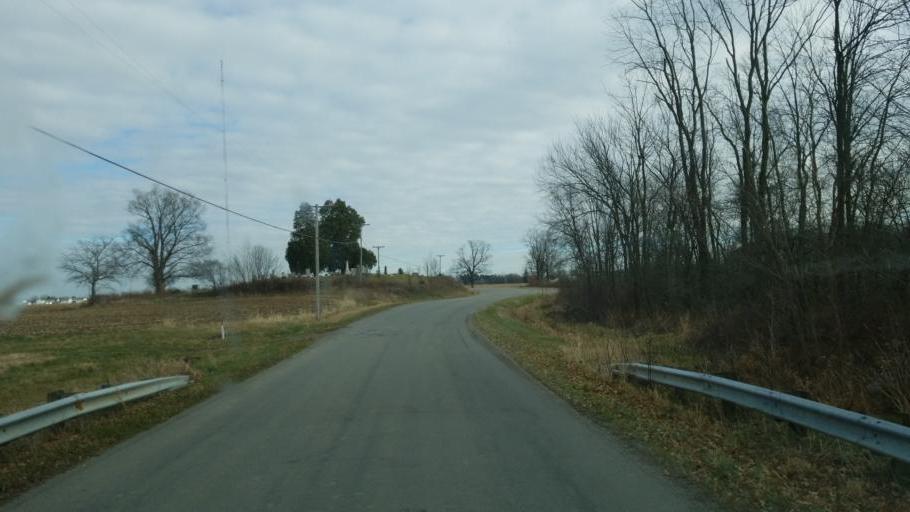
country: US
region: Ohio
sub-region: Crawford County
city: Crestline
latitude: 40.7698
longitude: -82.7607
